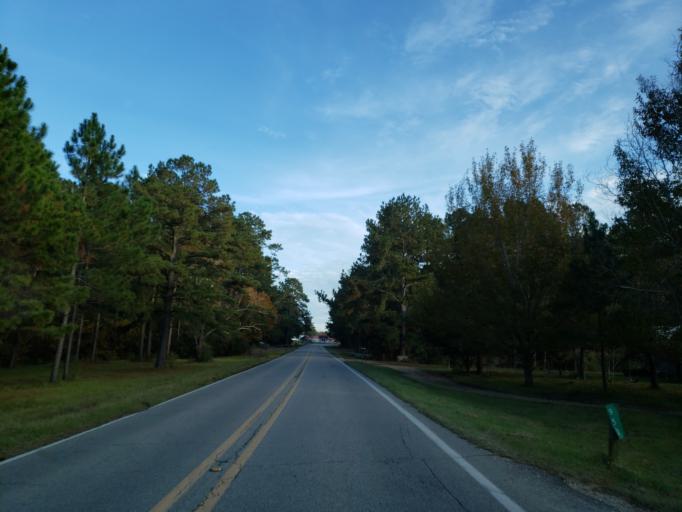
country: US
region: Mississippi
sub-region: Lamar County
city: Purvis
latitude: 31.1736
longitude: -89.4308
